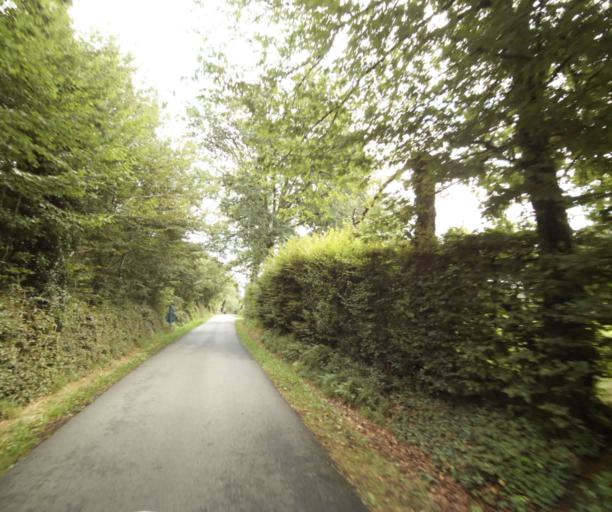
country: FR
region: Limousin
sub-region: Departement de la Correze
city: Sainte-Fortunade
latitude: 45.1964
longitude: 1.8256
